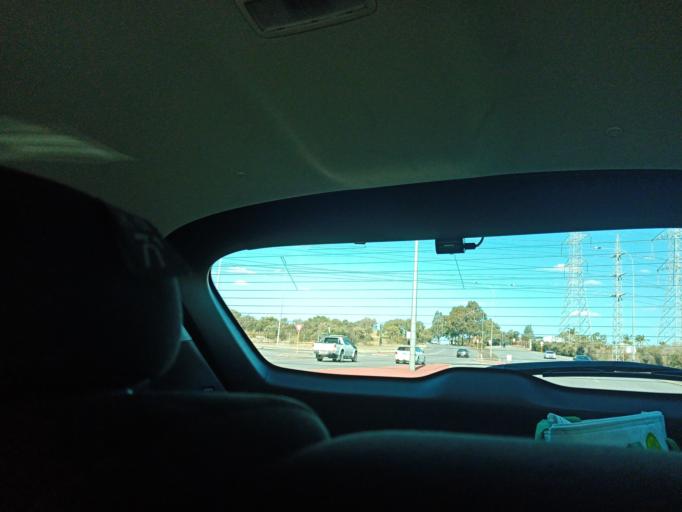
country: AU
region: Western Australia
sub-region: City of Cockburn
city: Success
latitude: -32.1295
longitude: 115.8486
